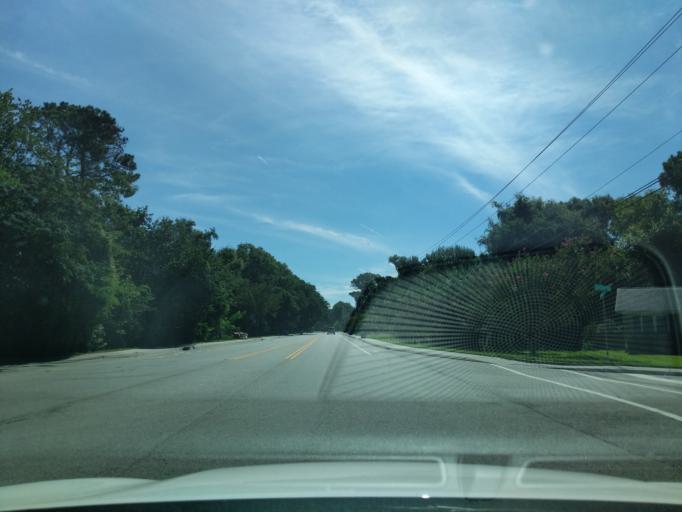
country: US
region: South Carolina
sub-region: Charleston County
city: Charleston
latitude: 32.7420
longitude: -79.9278
